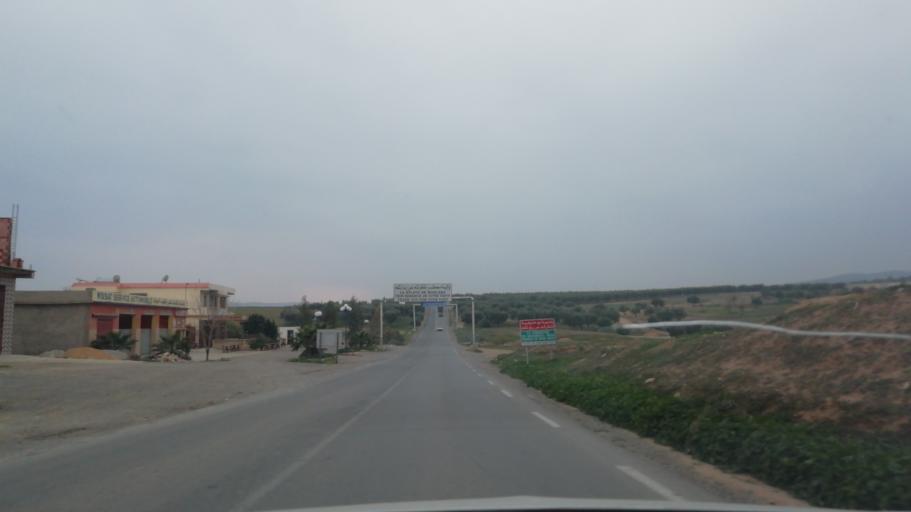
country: DZ
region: Mascara
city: Bou Hanifia el Hamamat
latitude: 35.2824
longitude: -0.1485
